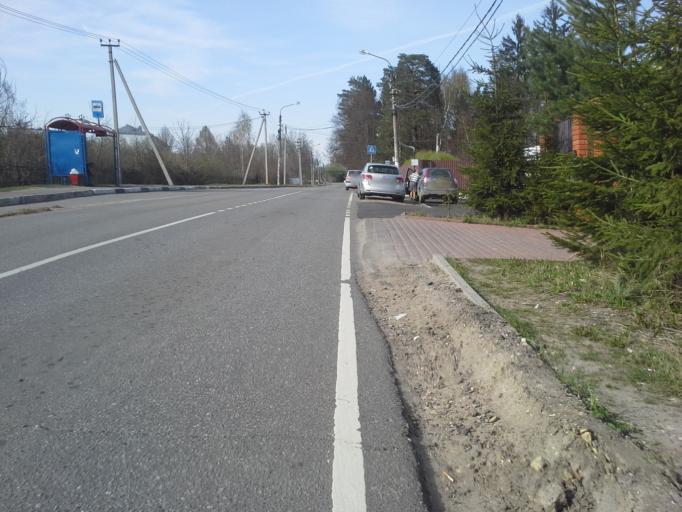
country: RU
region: Moskovskaya
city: Vatutinki
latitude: 55.4526
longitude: 37.3988
